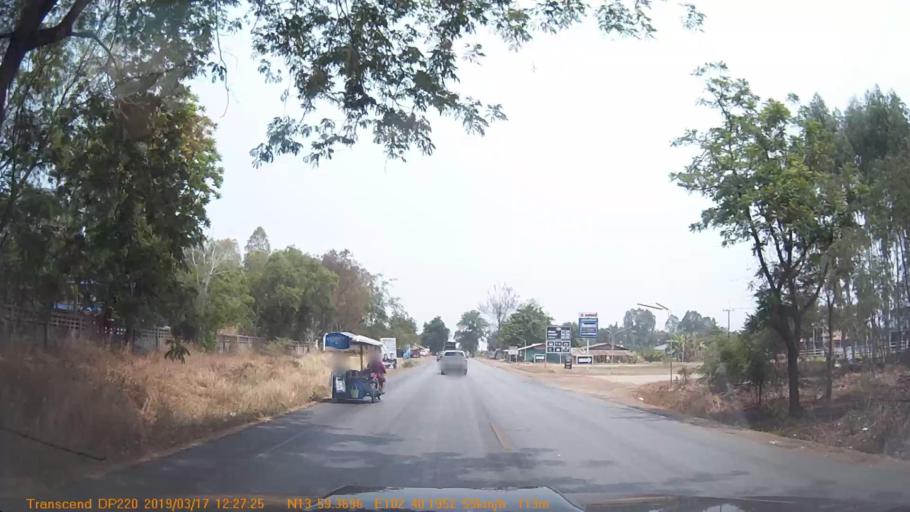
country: TH
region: Sa Kaeo
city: Ta Phraya
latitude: 13.9895
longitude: 102.6701
